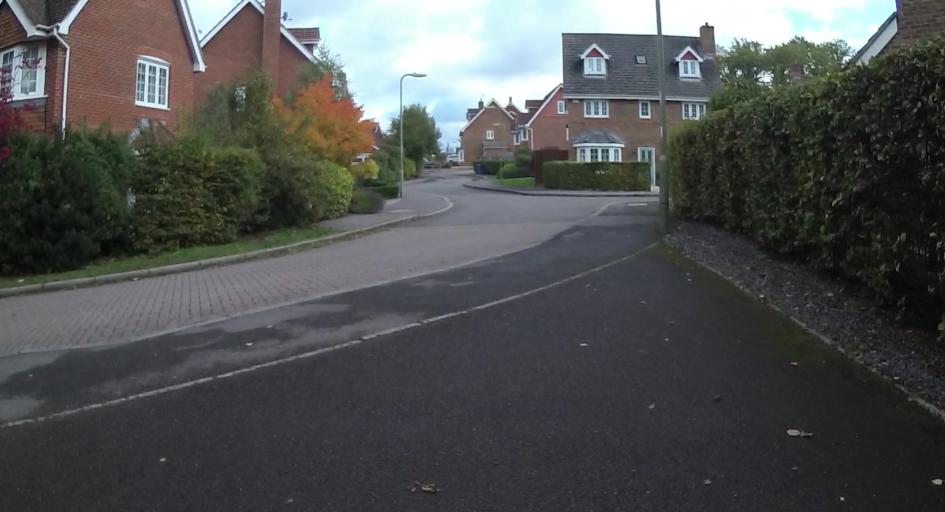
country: GB
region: England
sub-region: Hampshire
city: Fleet
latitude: 51.2928
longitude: -0.8668
